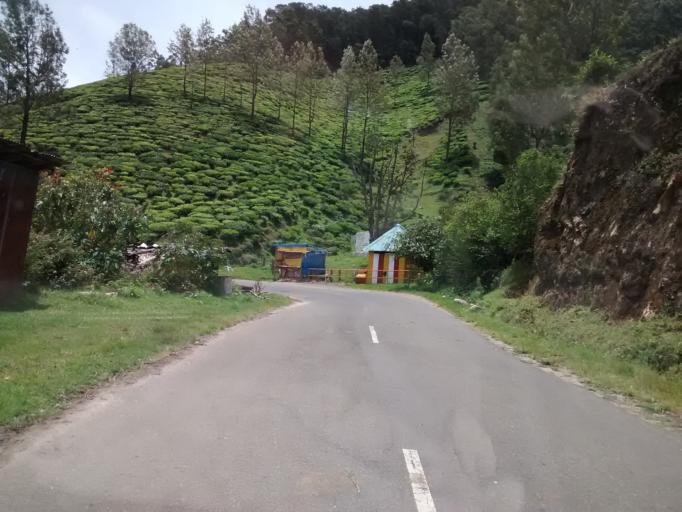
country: IN
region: Kerala
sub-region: Idukki
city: Munnar
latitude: 10.1354
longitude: 77.1799
